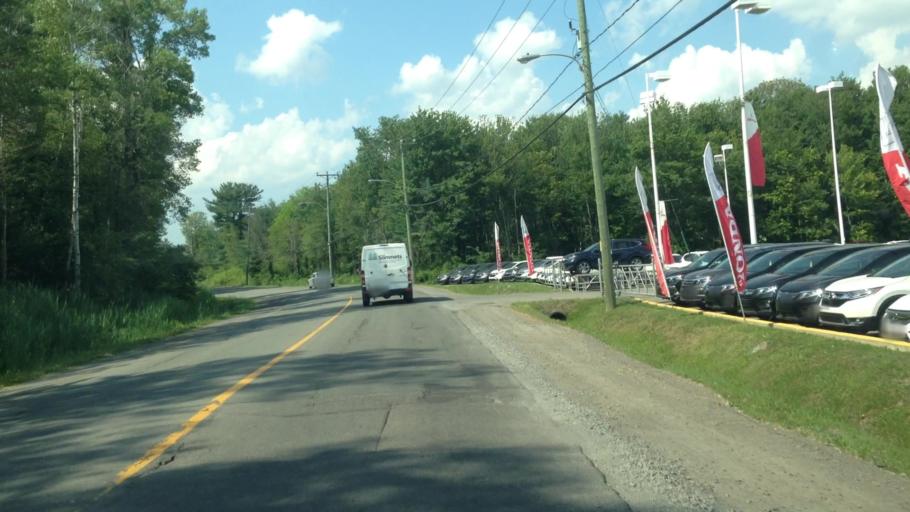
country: CA
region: Quebec
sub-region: Laurentides
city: Saint-Jerome
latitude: 45.7743
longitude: -74.0228
